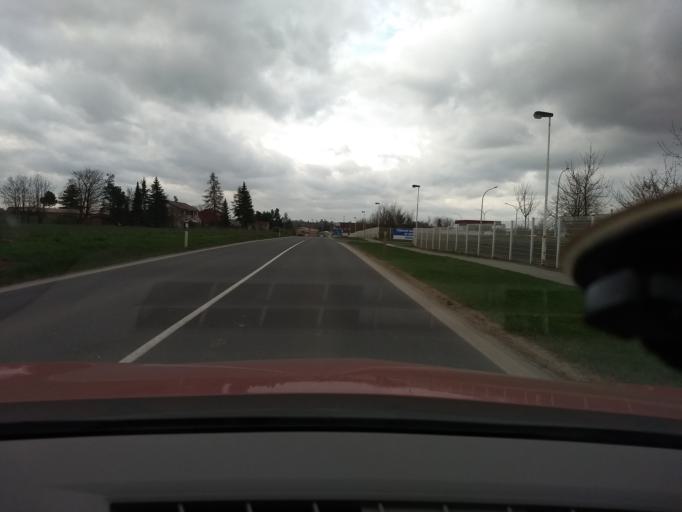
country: CZ
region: Central Bohemia
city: Unhost'
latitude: 50.1205
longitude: 14.1285
